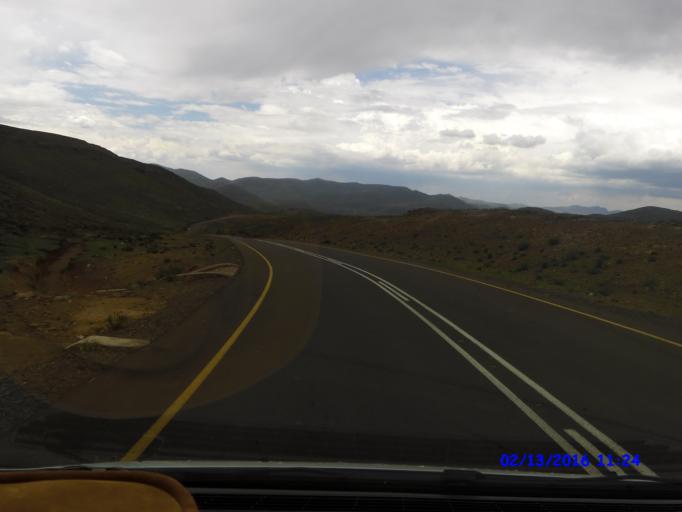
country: LS
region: Maseru
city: Nako
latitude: -29.7649
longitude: 27.9956
